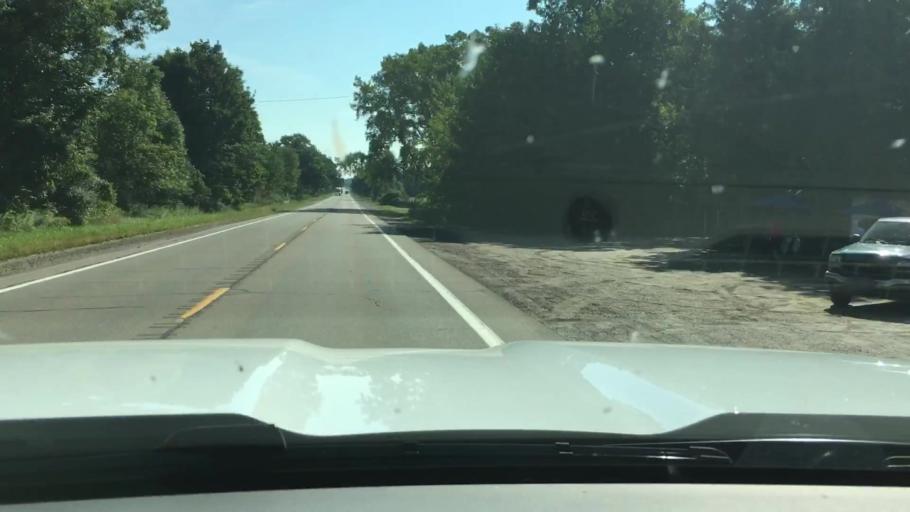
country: US
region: Michigan
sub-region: Gratiot County
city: Alma
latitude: 43.4082
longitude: -84.7640
